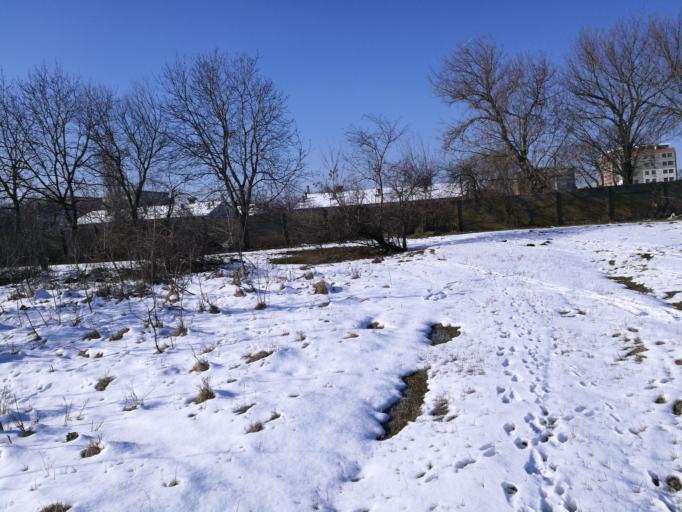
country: RO
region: Ilfov
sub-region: Comuna Otopeni
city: Otopeni
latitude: 44.5031
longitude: 26.0640
